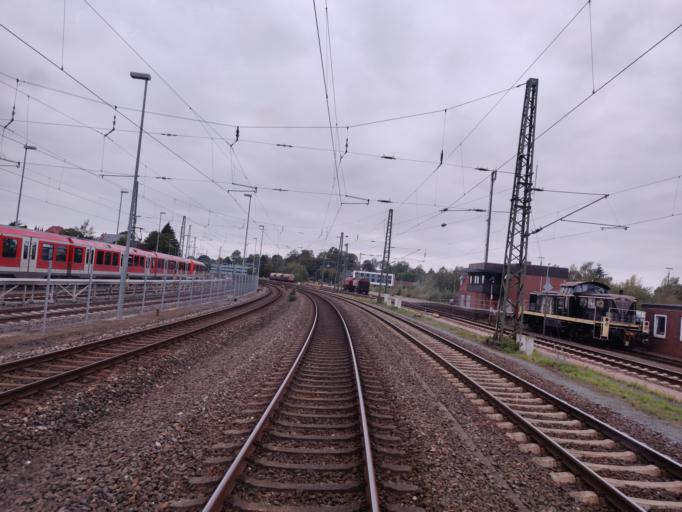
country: DE
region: Lower Saxony
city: Stade
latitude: 53.5945
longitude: 9.4860
